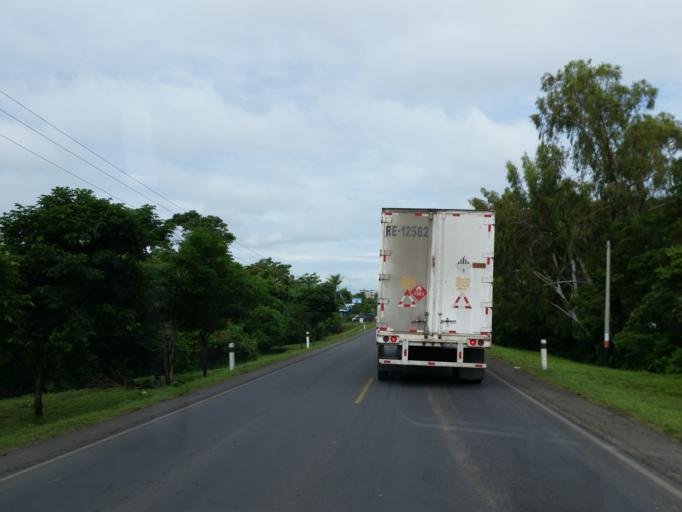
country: NI
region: Leon
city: Nagarote
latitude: 12.2692
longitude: -86.5538
